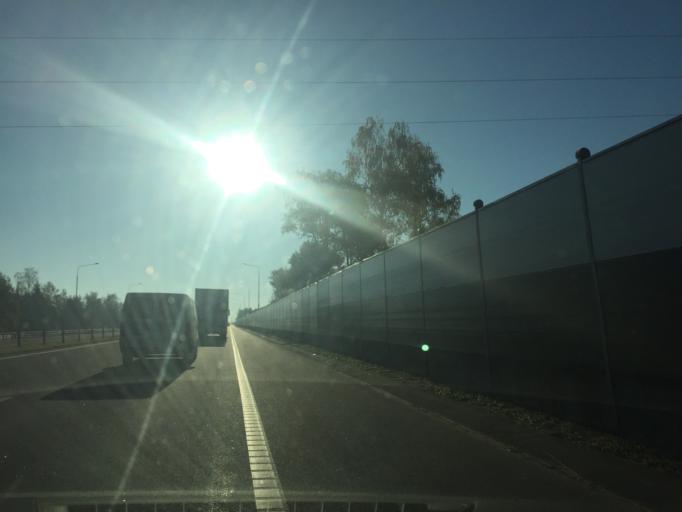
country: BY
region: Minsk
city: Luhavaya Slabada
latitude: 53.7862
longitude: 27.8317
